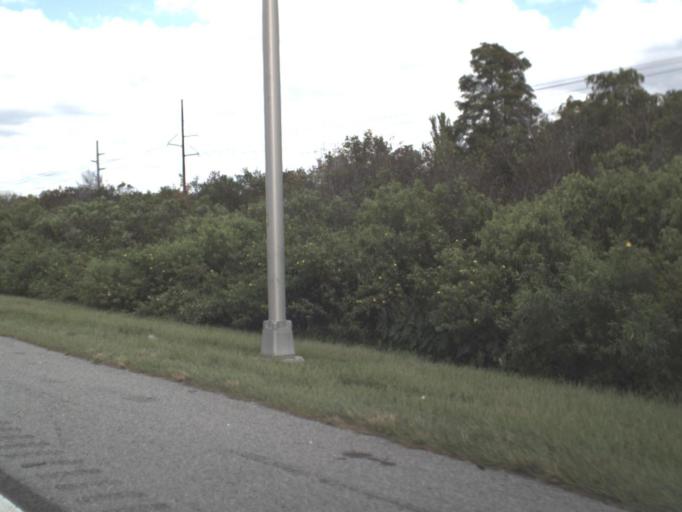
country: US
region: Florida
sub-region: Orange County
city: Oak Ridge
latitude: 28.4588
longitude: -81.4294
